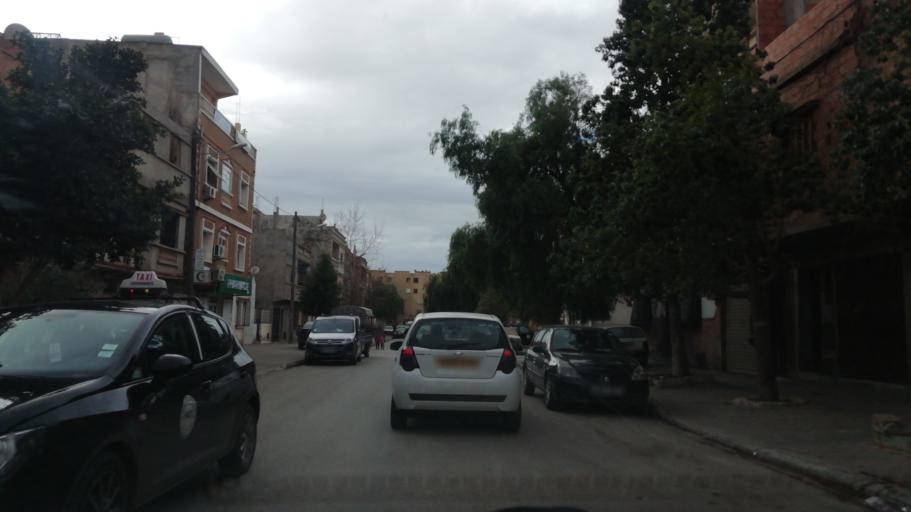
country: DZ
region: Oran
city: Oran
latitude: 35.6852
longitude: -0.5972
